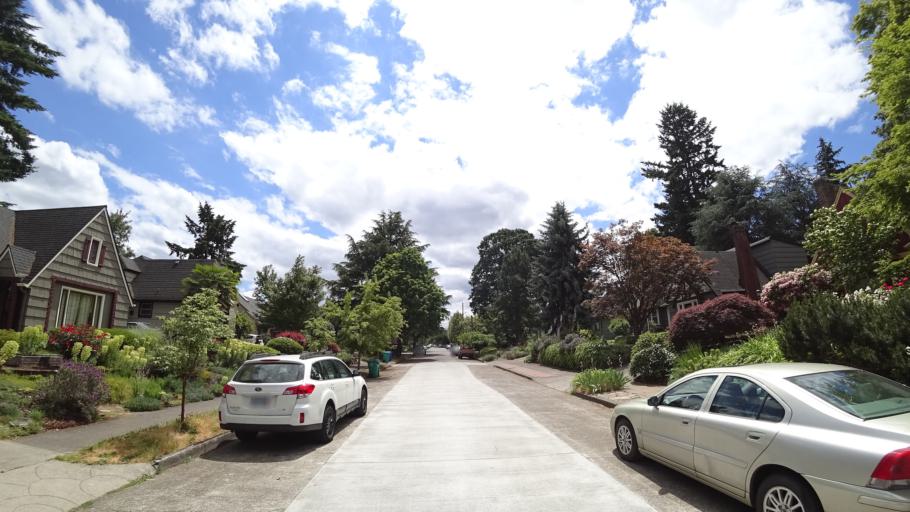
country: US
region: Oregon
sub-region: Multnomah County
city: Portland
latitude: 45.5671
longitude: -122.6759
